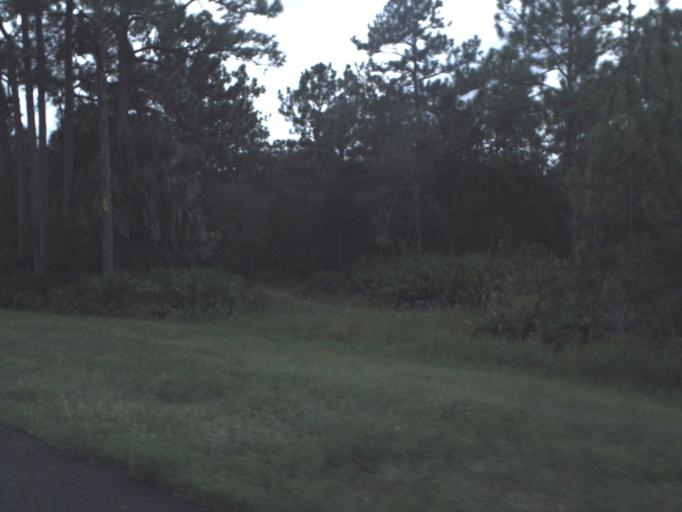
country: US
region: Florida
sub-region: Citrus County
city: Sugarmill Woods
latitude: 28.6802
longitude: -82.5525
